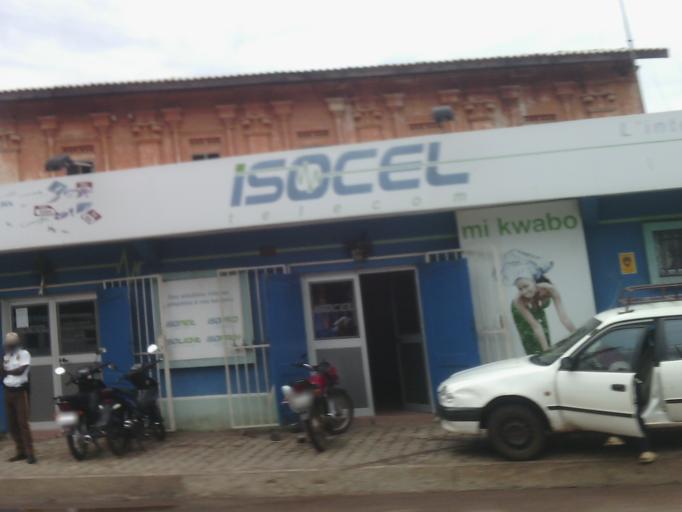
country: BJ
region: Queme
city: Porto-Novo
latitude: 6.4729
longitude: 2.6212
